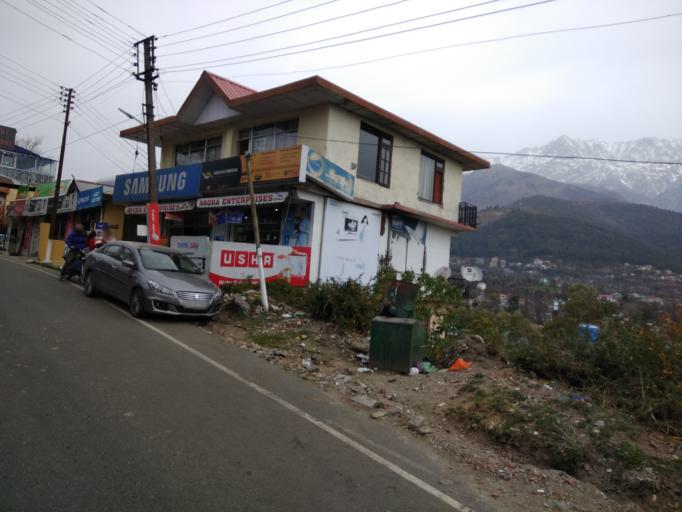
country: IN
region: Himachal Pradesh
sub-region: Kangra
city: Dharmsala
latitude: 32.2050
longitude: 76.3250
